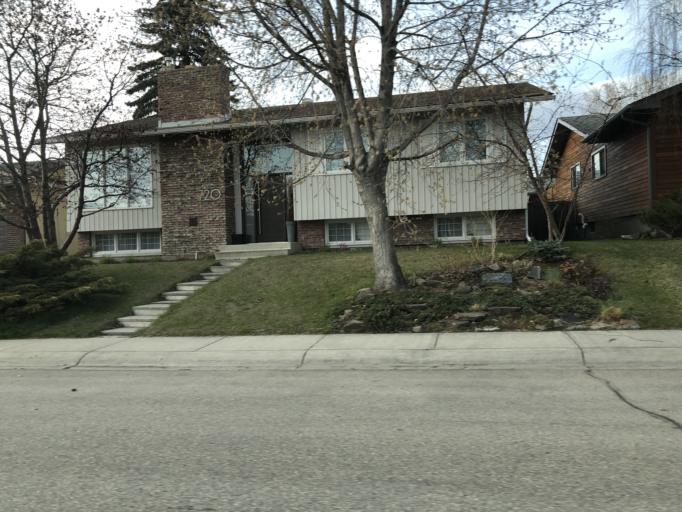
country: CA
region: Alberta
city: Calgary
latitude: 50.9325
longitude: -114.0451
